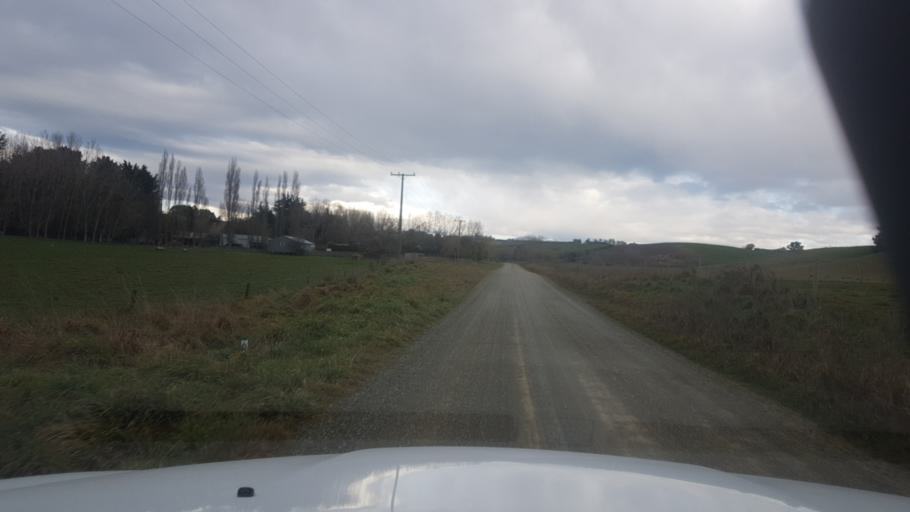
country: NZ
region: Canterbury
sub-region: Timaru District
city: Pleasant Point
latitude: -44.3393
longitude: 171.1738
